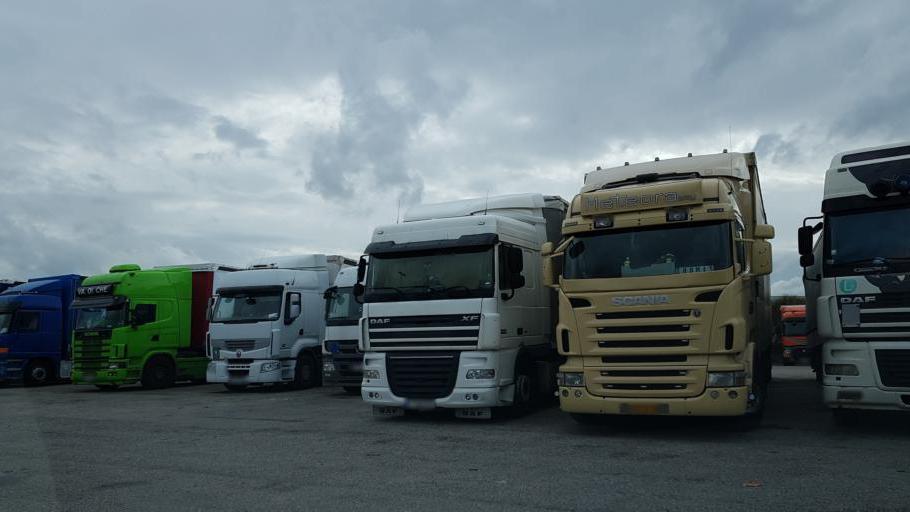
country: IT
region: Apulia
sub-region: Provincia di Brindisi
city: Materdomini
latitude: 40.6427
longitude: 17.9619
